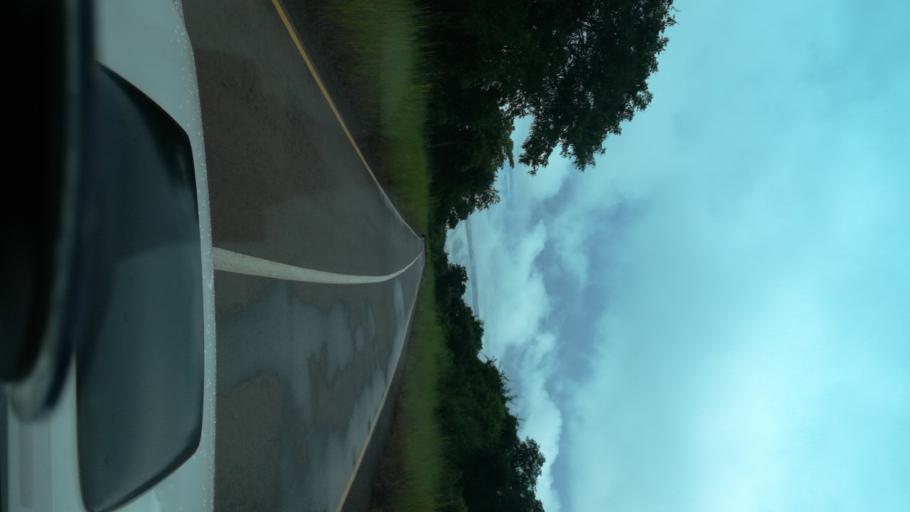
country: ZM
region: Luapula
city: Mansa
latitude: -10.9483
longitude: 28.1752
